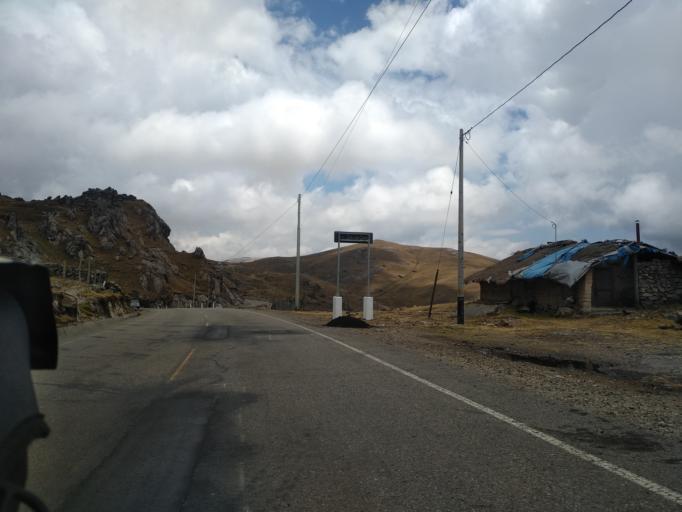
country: PE
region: La Libertad
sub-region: Provincia de Santiago de Chuco
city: Quiruvilca
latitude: -7.9739
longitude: -78.2147
